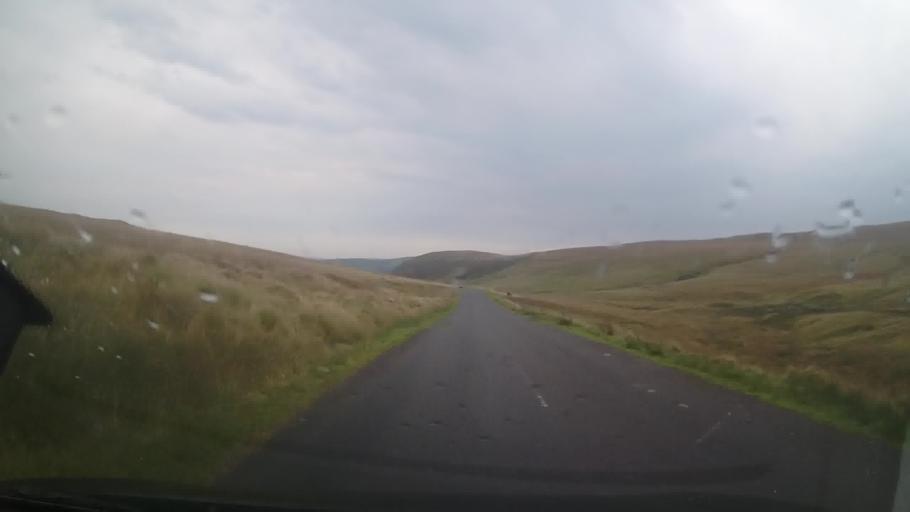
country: GB
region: Wales
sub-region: Sir Powys
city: Rhayader
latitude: 52.3188
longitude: -3.5761
